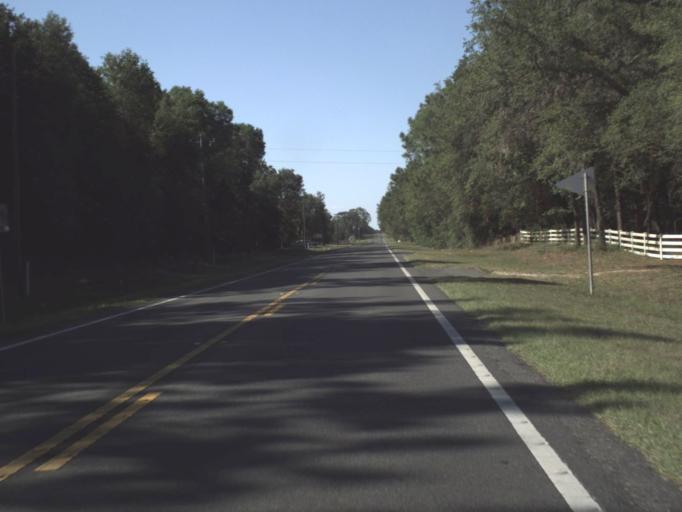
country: US
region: Florida
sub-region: Marion County
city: Dunnellon
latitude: 29.1646
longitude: -82.4402
